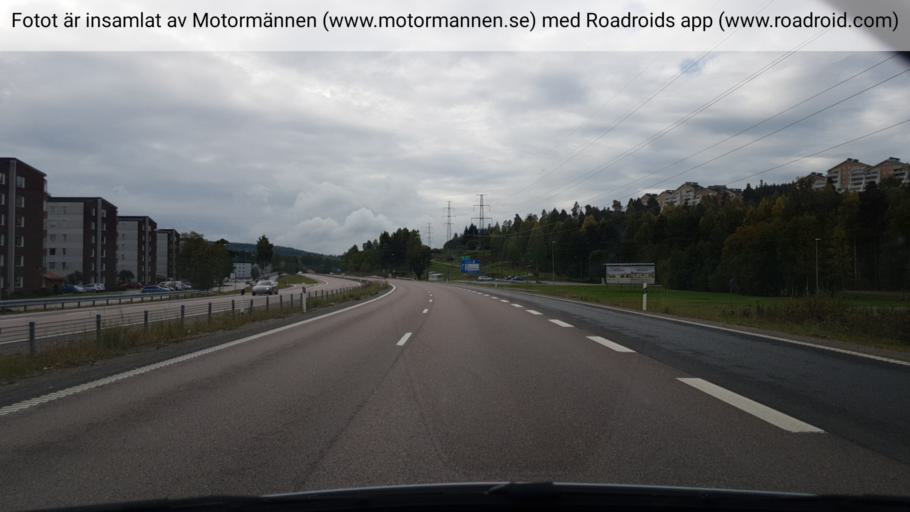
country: SE
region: Vaesternorrland
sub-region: Timra Kommun
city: Timra
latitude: 62.4906
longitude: 17.3261
